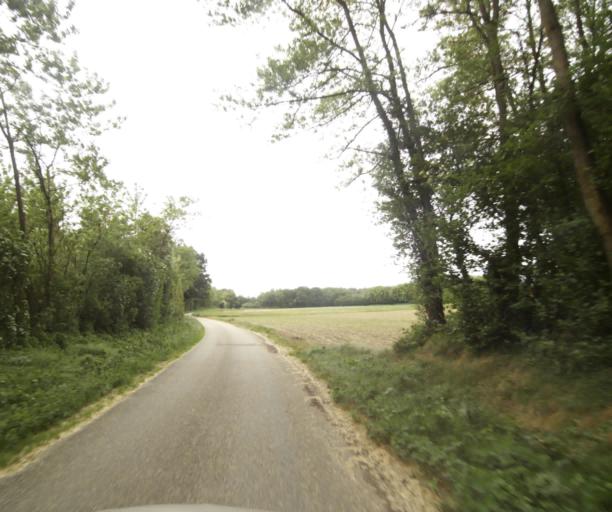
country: FR
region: Rhone-Alpes
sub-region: Departement de l'Ain
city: Mionnay
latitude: 45.8654
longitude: 4.9312
